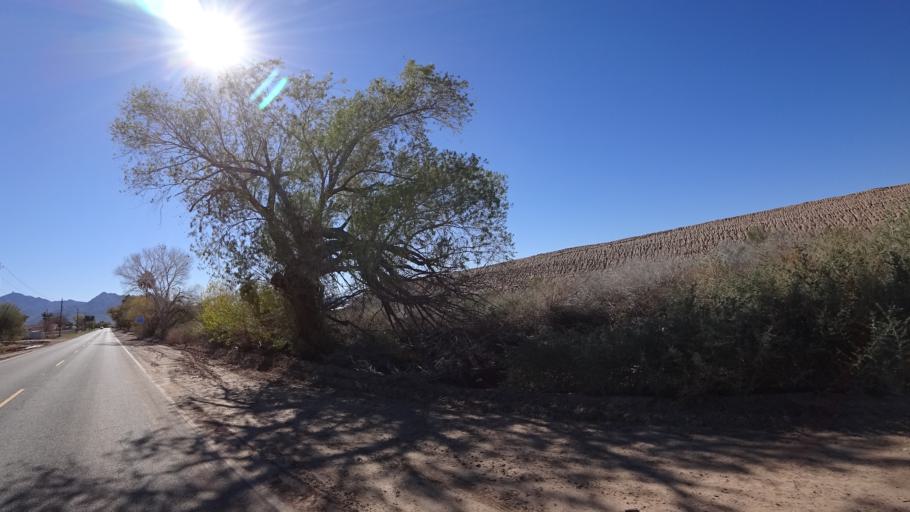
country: US
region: Arizona
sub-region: Maricopa County
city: Avondale
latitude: 33.3965
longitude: -112.3405
